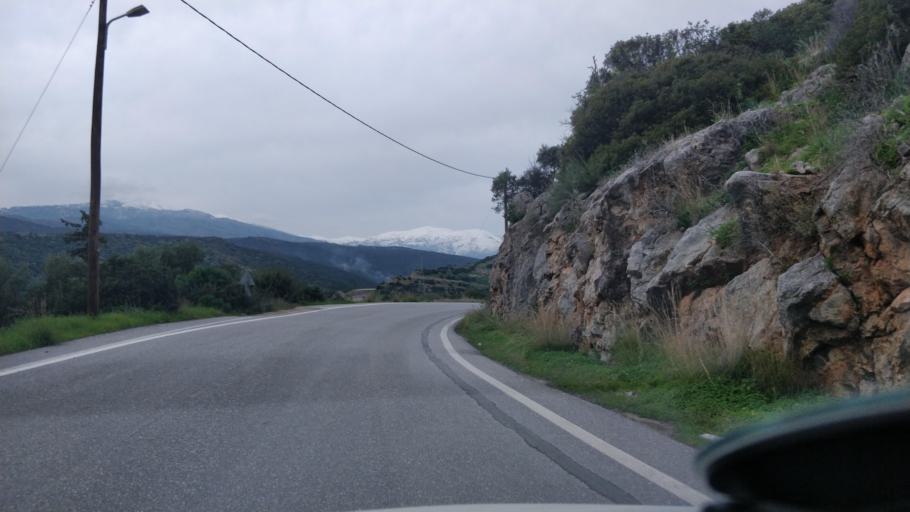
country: GR
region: Crete
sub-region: Nomos Lasithiou
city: Agios Nikolaos
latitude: 35.1179
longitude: 25.7274
